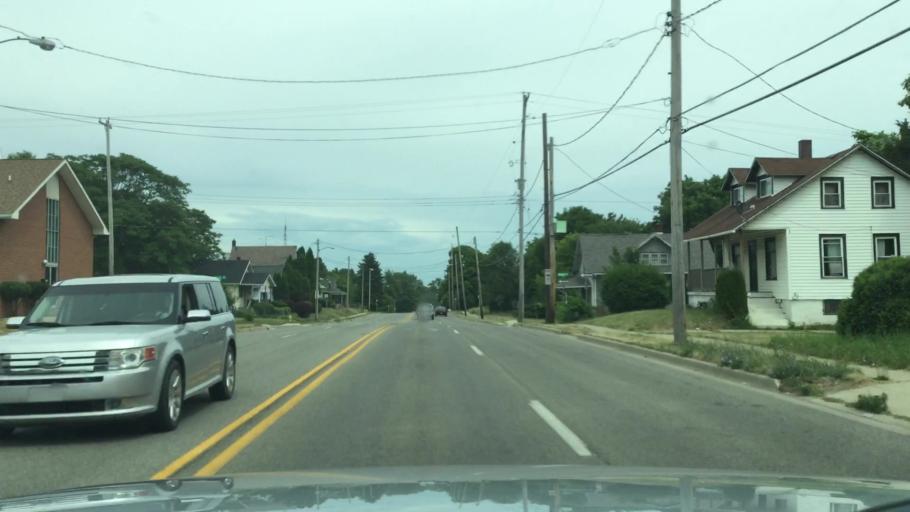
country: US
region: Michigan
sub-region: Genesee County
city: Beecher
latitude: 43.0611
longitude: -83.6914
